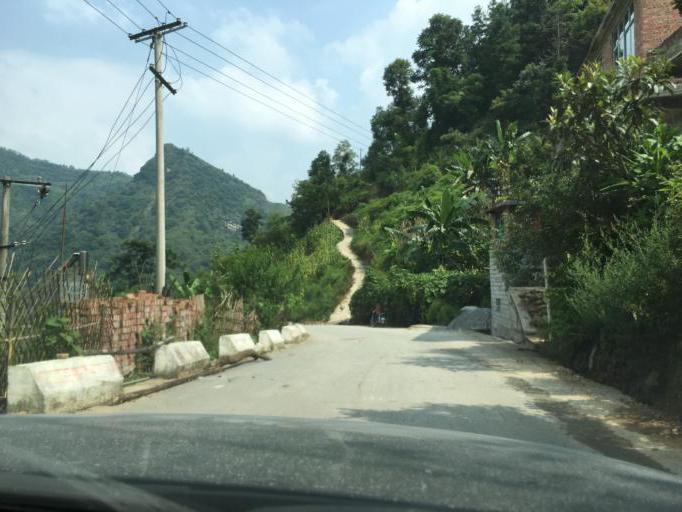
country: CN
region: Guangxi Zhuangzu Zizhiqu
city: Tongle
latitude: 25.2949
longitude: 106.2668
